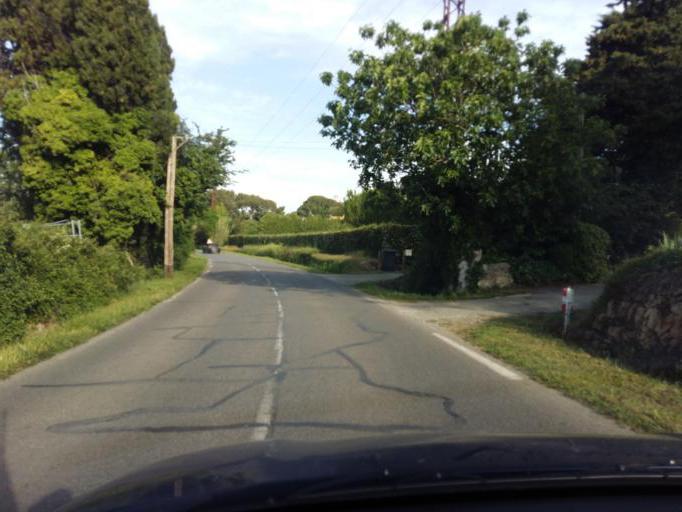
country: FR
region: Provence-Alpes-Cote d'Azur
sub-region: Departement des Bouches-du-Rhone
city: Pelissanne
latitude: 43.6355
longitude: 5.1279
